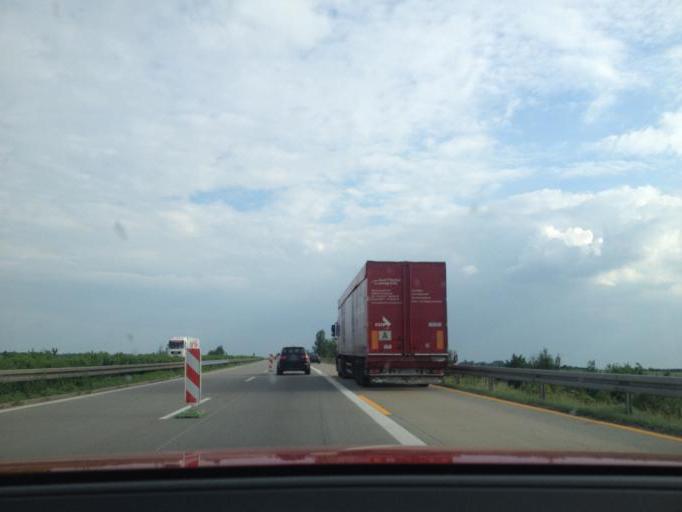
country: DE
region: Saxony-Anhalt
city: Nauendorf
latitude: 51.6020
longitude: 11.8703
